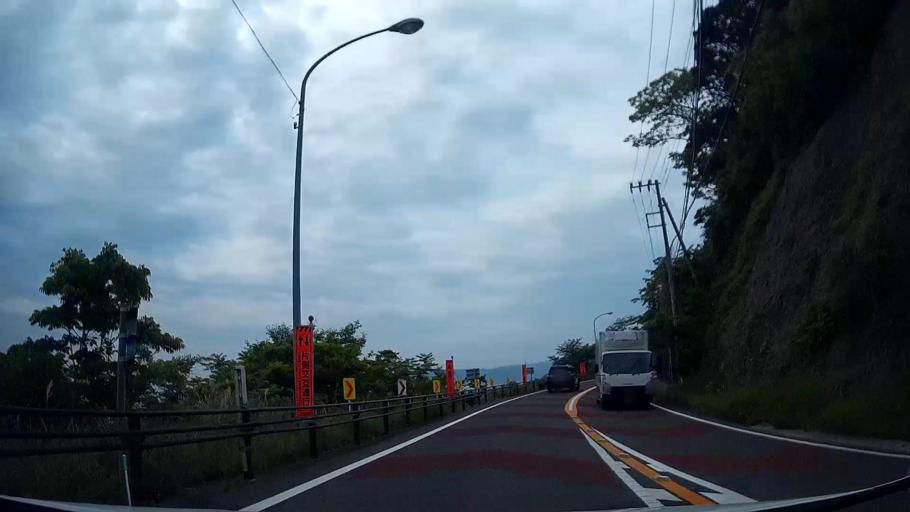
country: JP
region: Shizuoka
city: Ito
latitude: 35.0262
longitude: 139.0984
